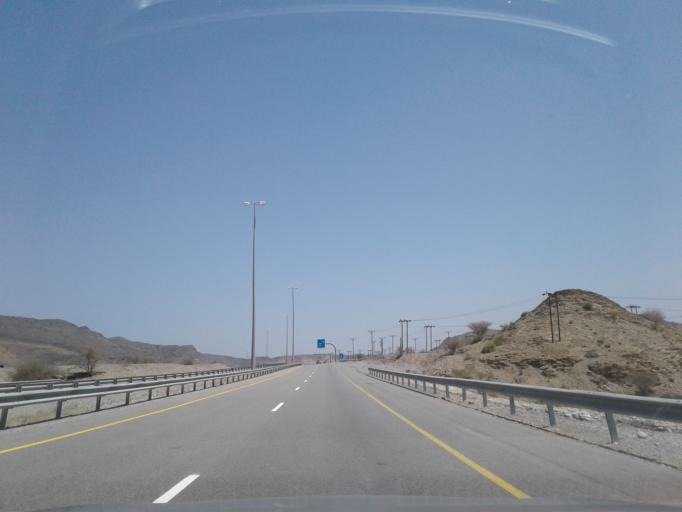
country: OM
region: Muhafazat Masqat
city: Muscat
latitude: 23.2500
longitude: 58.7840
